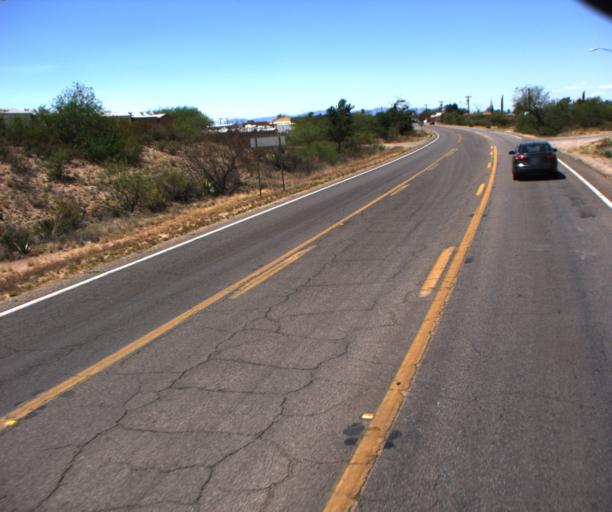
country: US
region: Arizona
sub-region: Cochise County
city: Tombstone
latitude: 31.7099
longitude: -110.0567
